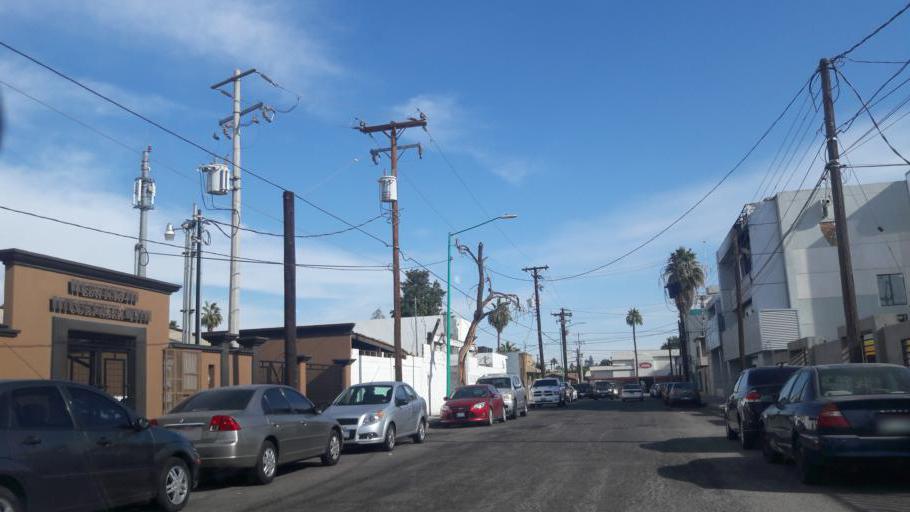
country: MX
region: Baja California
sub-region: Mexicali
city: Mexicali
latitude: 32.6514
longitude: -115.4518
